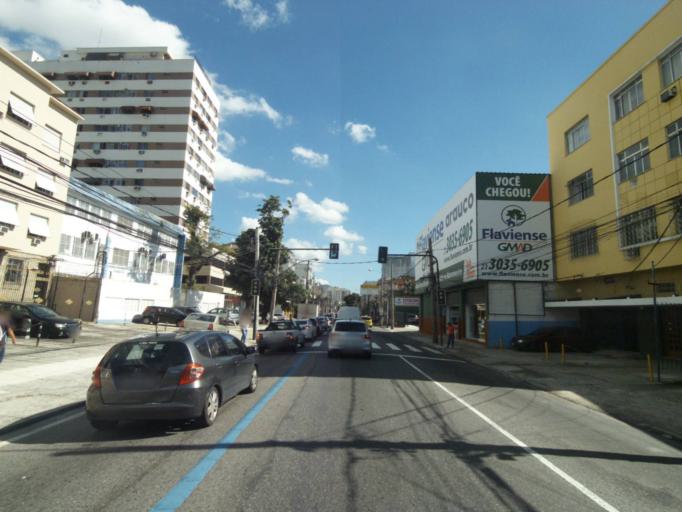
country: BR
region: Rio de Janeiro
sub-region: Rio De Janeiro
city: Rio de Janeiro
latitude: -22.9014
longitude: -43.2505
